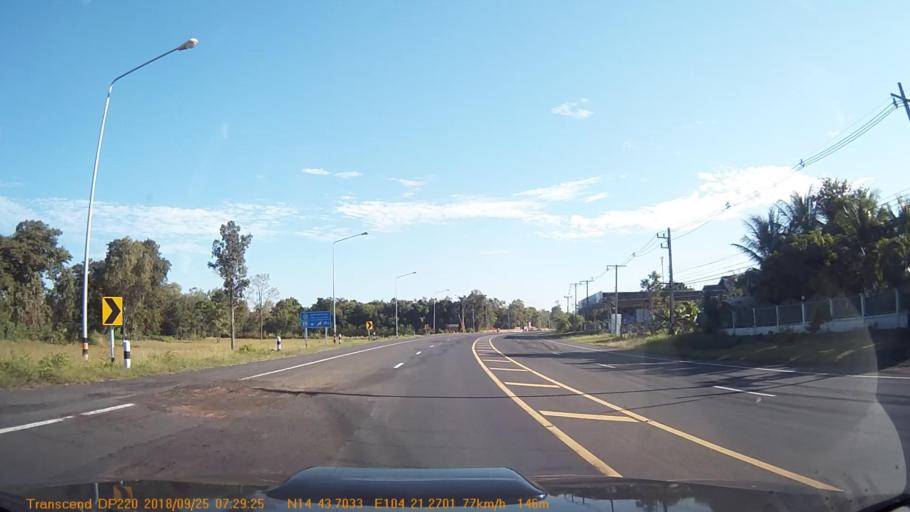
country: TH
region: Sisaket
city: Phrai Bueng
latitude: 14.7290
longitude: 104.3546
